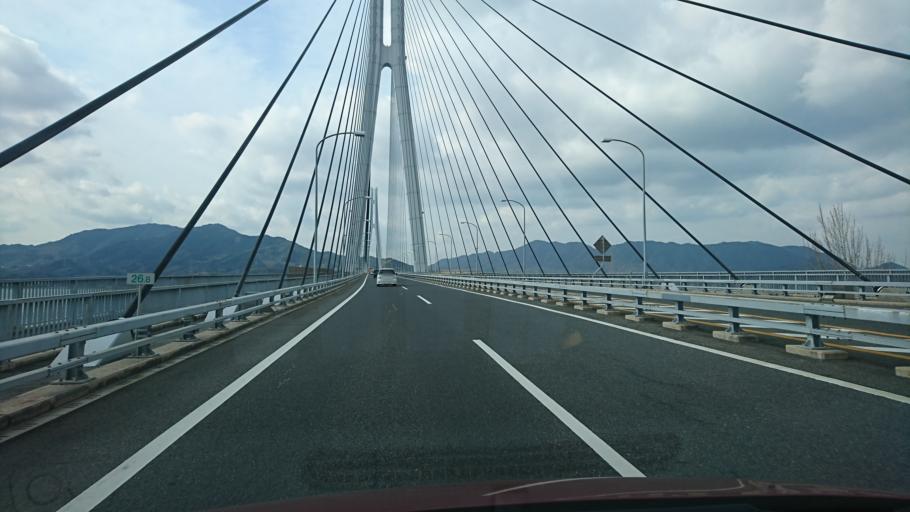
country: JP
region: Hiroshima
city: Innoshima
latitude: 34.2613
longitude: 133.0723
